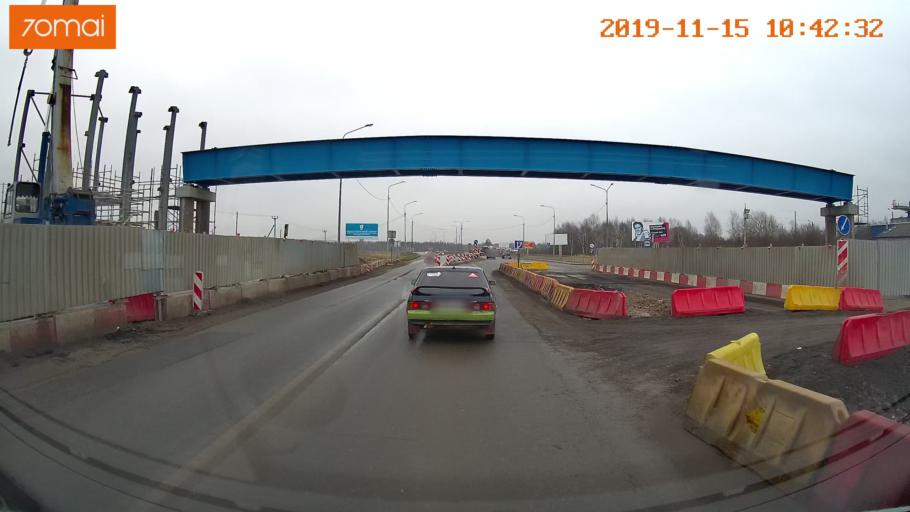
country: RU
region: Vologda
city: Sheksna
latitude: 59.2109
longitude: 38.5194
